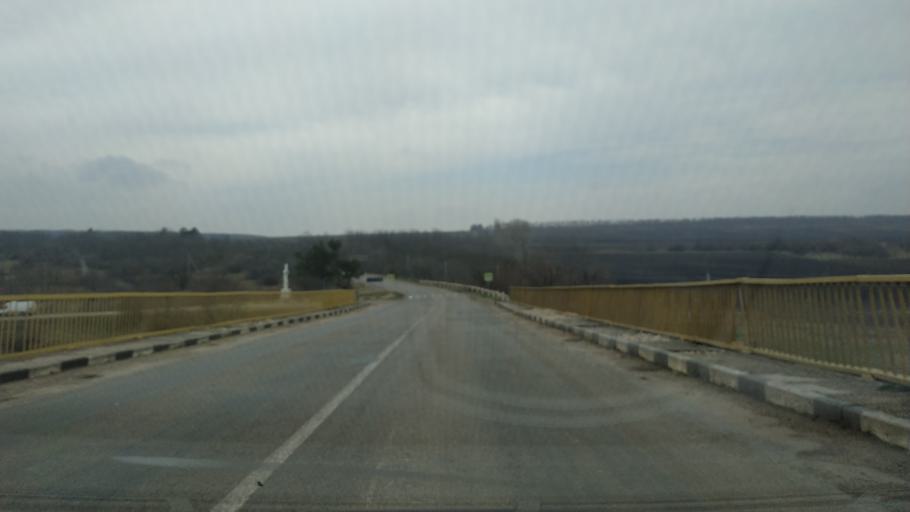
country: MD
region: Cahul
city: Cahul
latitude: 45.9552
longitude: 28.3484
